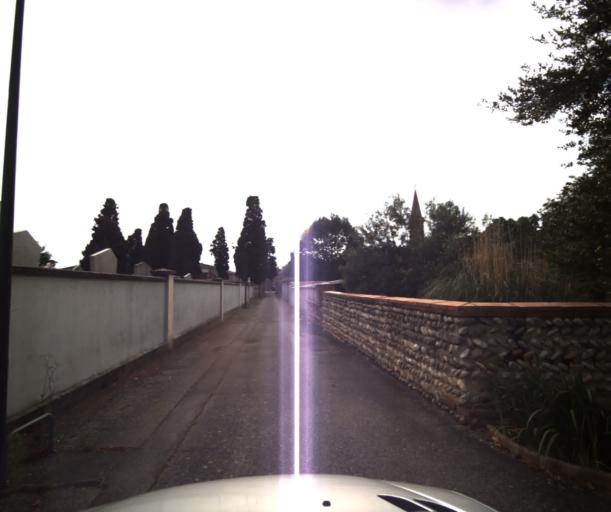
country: FR
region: Midi-Pyrenees
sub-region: Departement de la Haute-Garonne
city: Labarthe-sur-Leze
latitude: 43.4515
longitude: 1.4005
